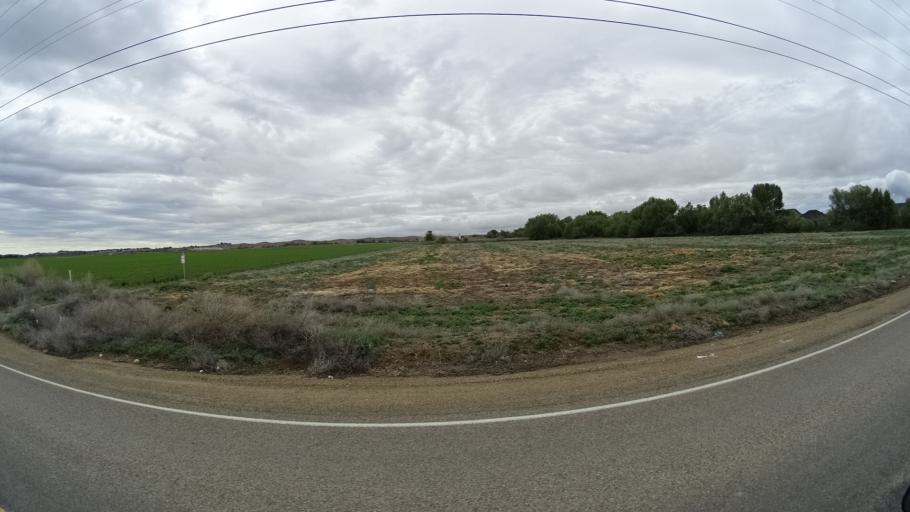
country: US
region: Idaho
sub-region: Ada County
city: Star
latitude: 43.7075
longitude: -116.4357
